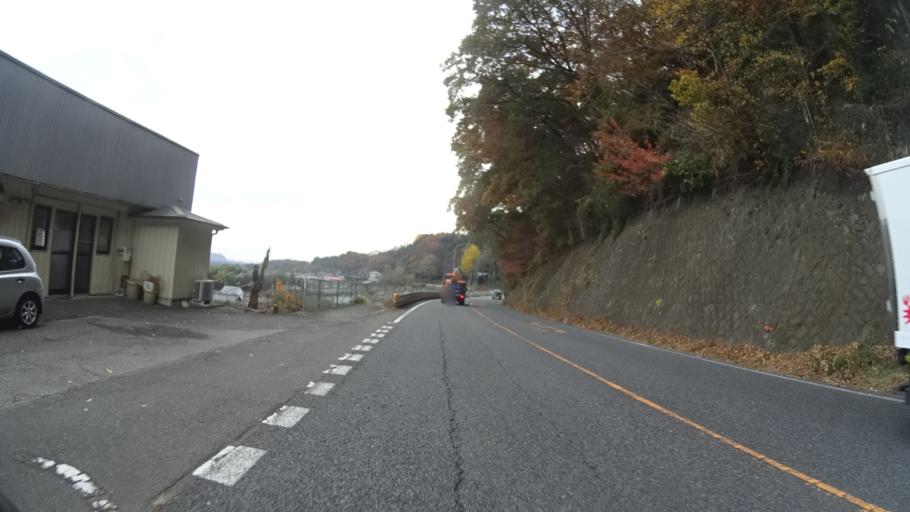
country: JP
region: Gunma
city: Shibukawa
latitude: 36.5534
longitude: 139.0310
